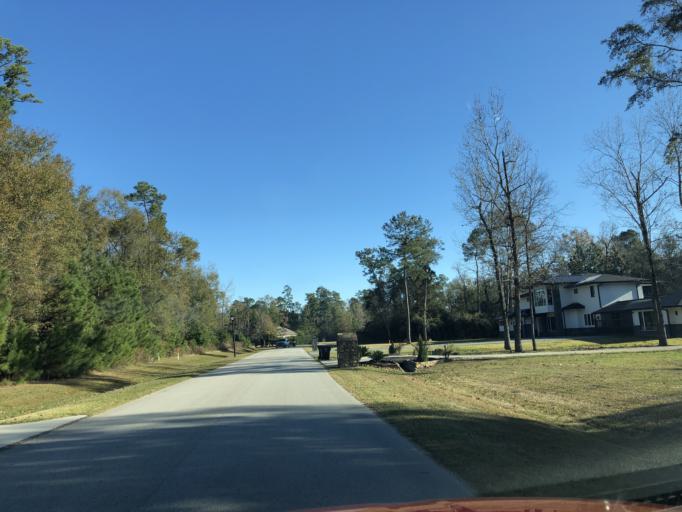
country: US
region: Texas
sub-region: Montgomery County
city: Porter Heights
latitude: 30.0812
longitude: -95.3358
